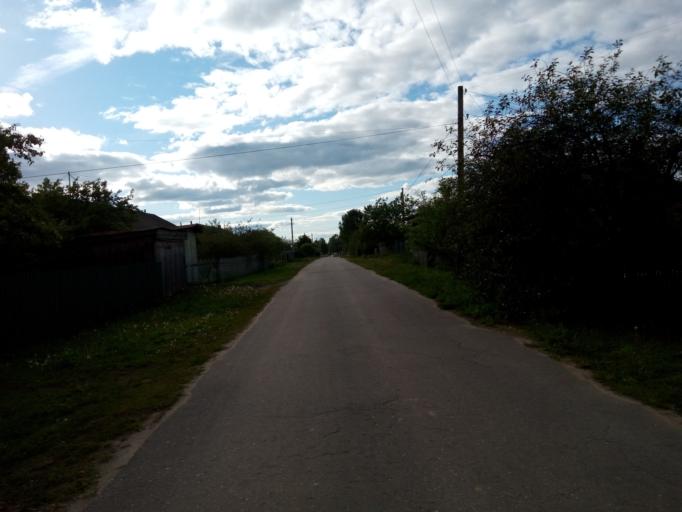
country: RU
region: Nizjnij Novgorod
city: Voskresenskoye
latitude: 56.7805
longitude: 45.5201
